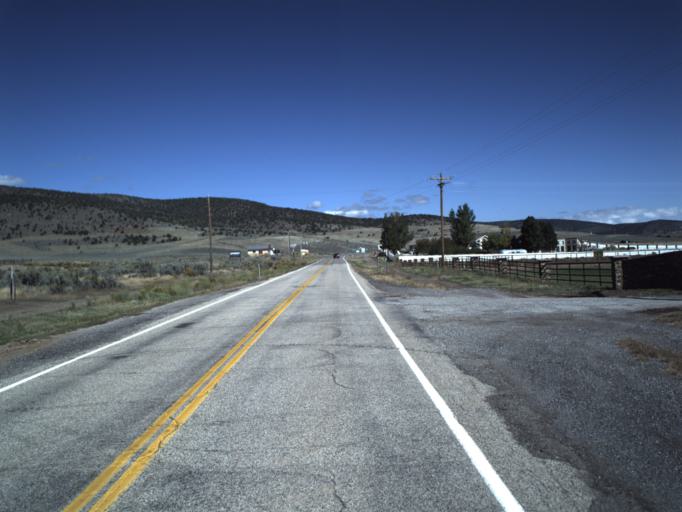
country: US
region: Utah
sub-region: Wayne County
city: Loa
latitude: 38.5168
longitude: -111.8814
